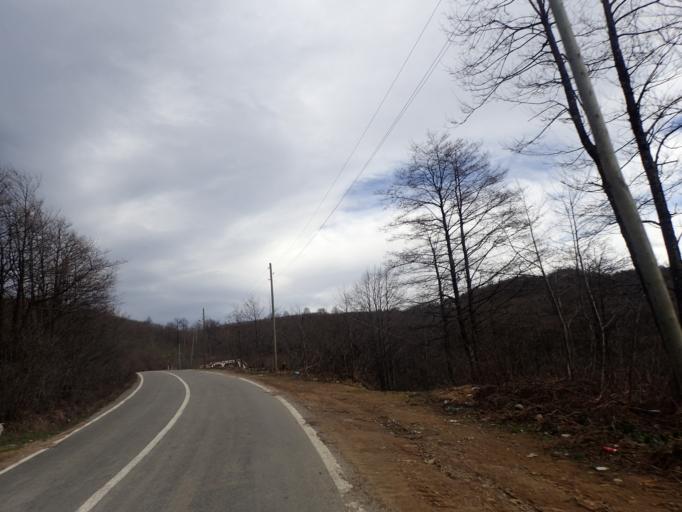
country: TR
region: Ordu
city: Camas
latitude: 40.8881
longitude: 37.5272
